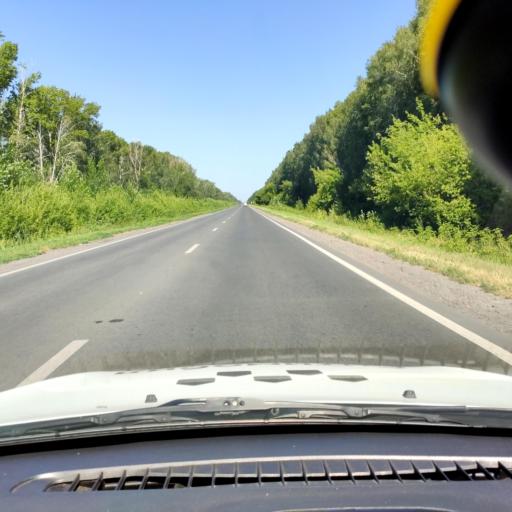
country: RU
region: Samara
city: Tol'yatti
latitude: 53.6023
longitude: 49.3216
